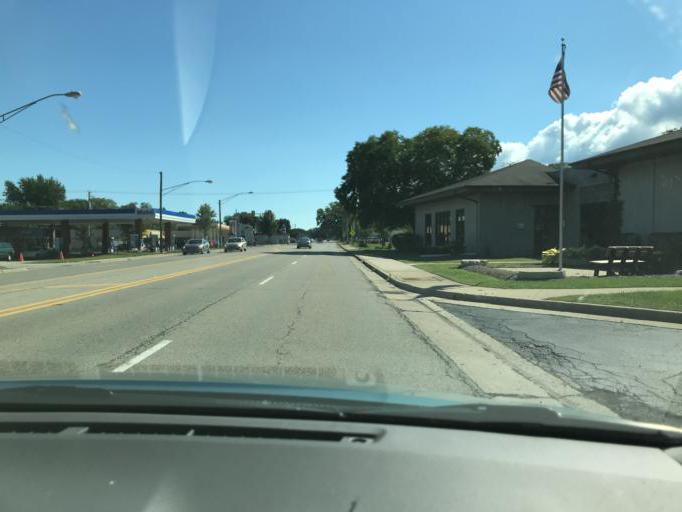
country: US
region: Illinois
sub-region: Lake County
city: Winthrop Harbor
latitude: 42.4801
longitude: -87.8235
